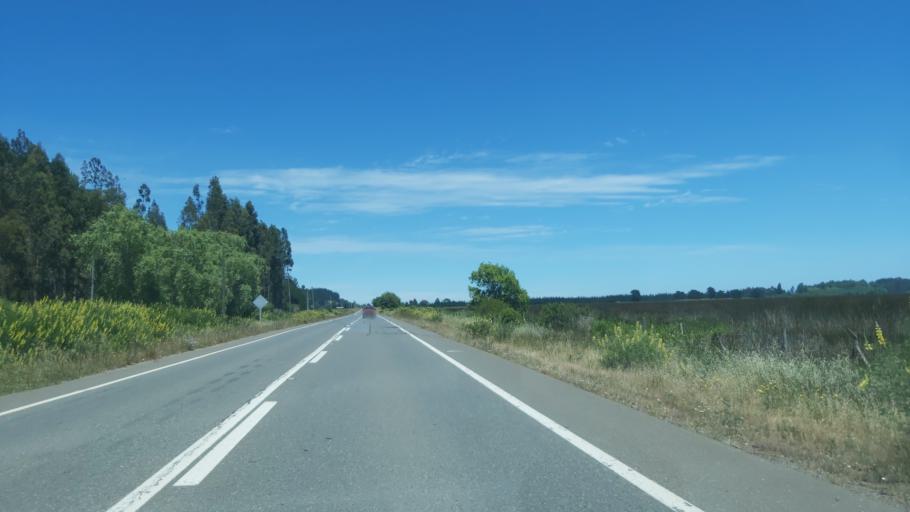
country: CL
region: Maule
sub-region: Provincia de Talca
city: Constitucion
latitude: -35.1596
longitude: -72.2538
